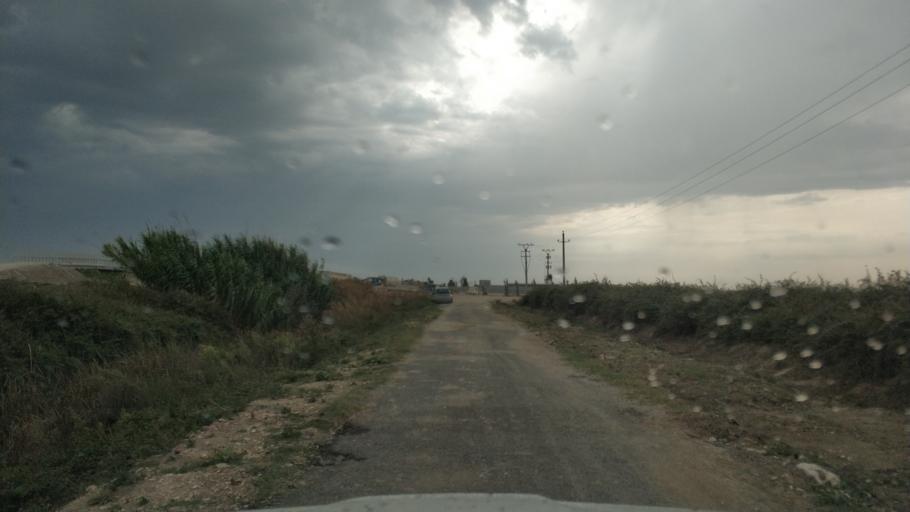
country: AL
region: Fier
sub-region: Rrethi i Fierit
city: Topoje
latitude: 40.7116
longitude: 19.4480
